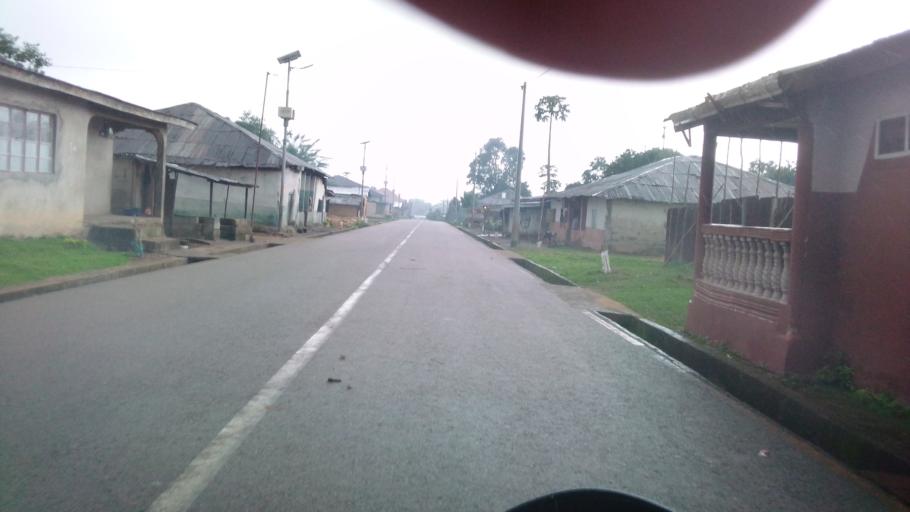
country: SL
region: Northern Province
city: Lunsar
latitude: 8.6839
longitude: -12.5307
